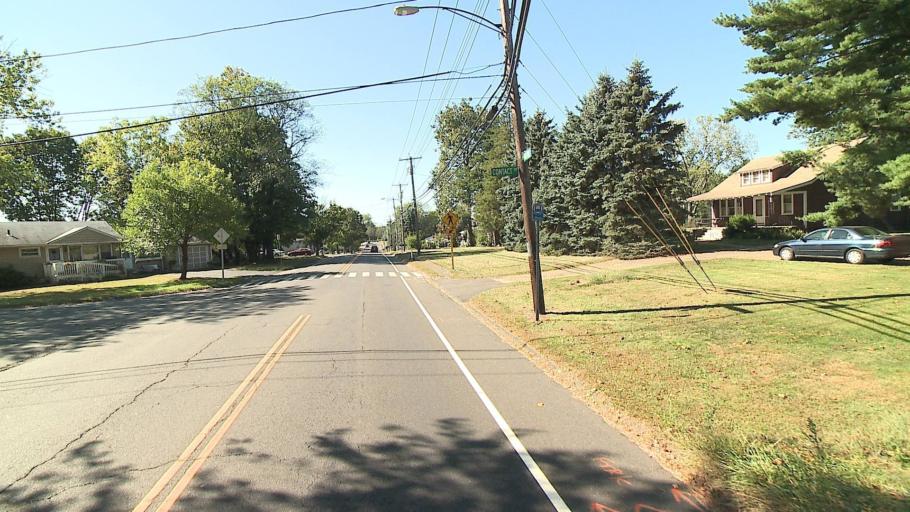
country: US
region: Connecticut
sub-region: New Haven County
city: Woodmont
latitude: 41.2416
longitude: -72.9833
